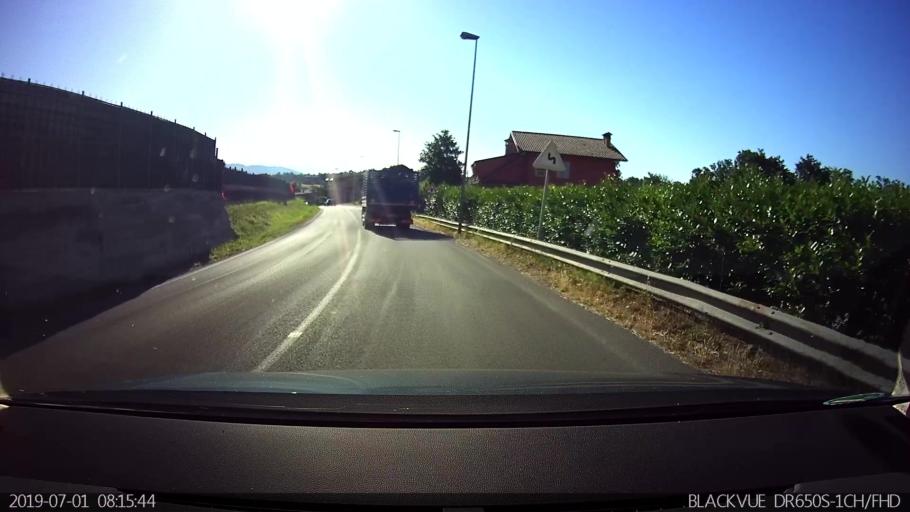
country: IT
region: Latium
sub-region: Provincia di Frosinone
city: Veroli
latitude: 41.7001
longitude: 13.4298
